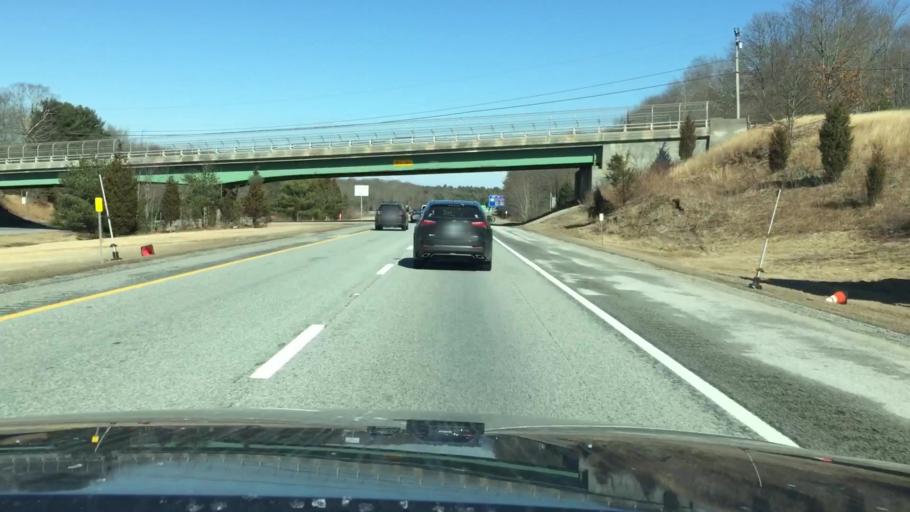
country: US
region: Rhode Island
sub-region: Kent County
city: West Greenwich
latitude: 41.5843
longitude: -71.6662
